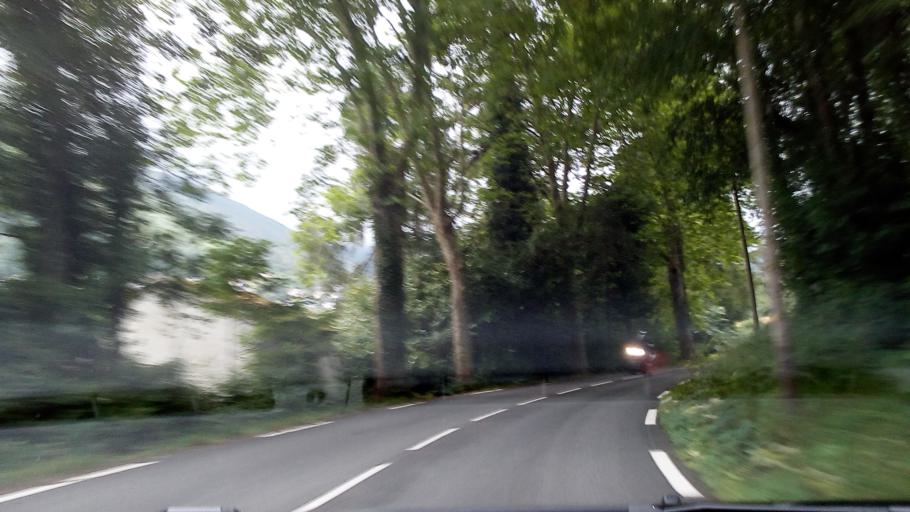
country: FR
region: Aquitaine
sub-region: Departement des Pyrenees-Atlantiques
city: Laruns
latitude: 42.9784
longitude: -0.4108
